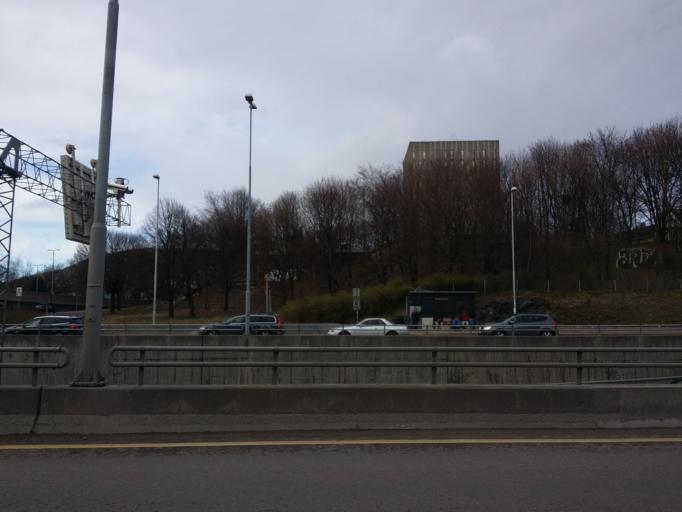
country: NO
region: Oslo
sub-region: Oslo
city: Oslo
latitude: 59.9370
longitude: 10.7858
